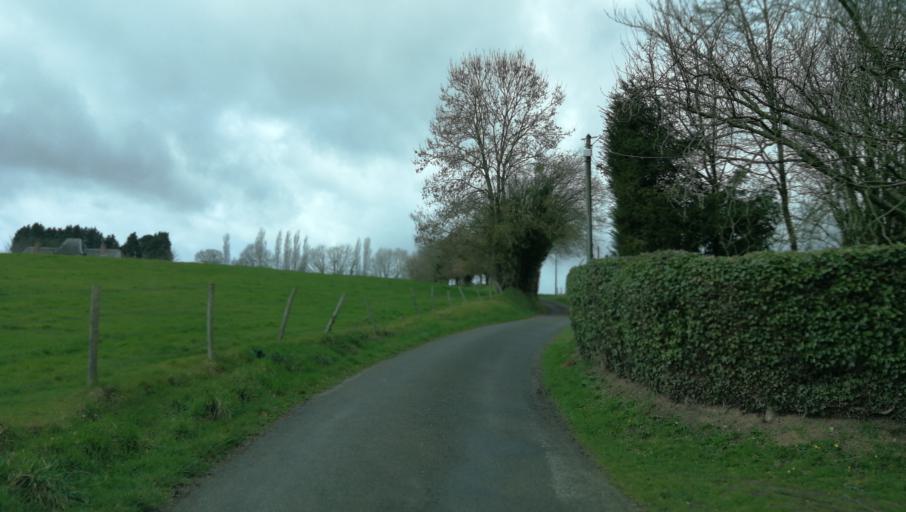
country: FR
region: Haute-Normandie
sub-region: Departement de l'Eure
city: Lieurey
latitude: 49.2337
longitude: 0.5273
